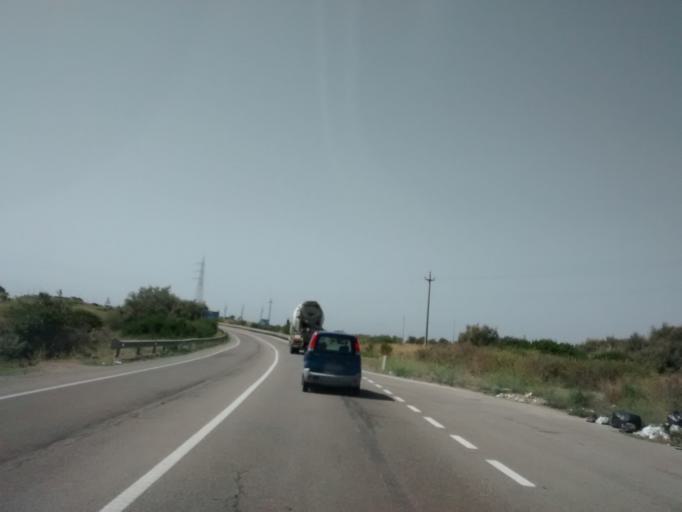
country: IT
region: Sardinia
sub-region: Provincia di Cagliari
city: Settimo San Pietro
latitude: 39.2690
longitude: 9.2019
